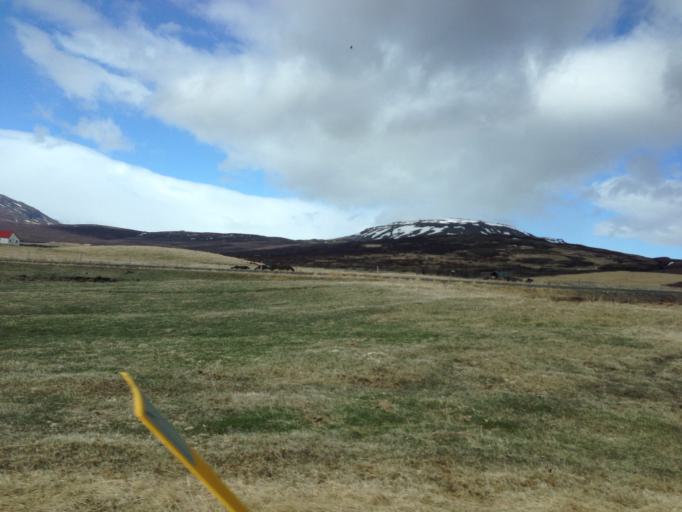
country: IS
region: South
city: Selfoss
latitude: 64.2766
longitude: -20.4153
